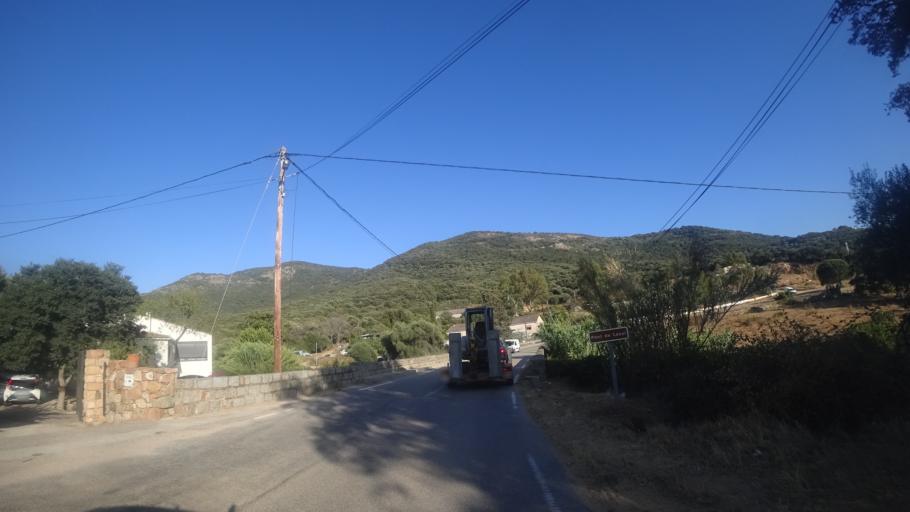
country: FR
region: Corsica
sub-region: Departement de la Corse-du-Sud
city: Cargese
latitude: 42.1555
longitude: 8.6072
